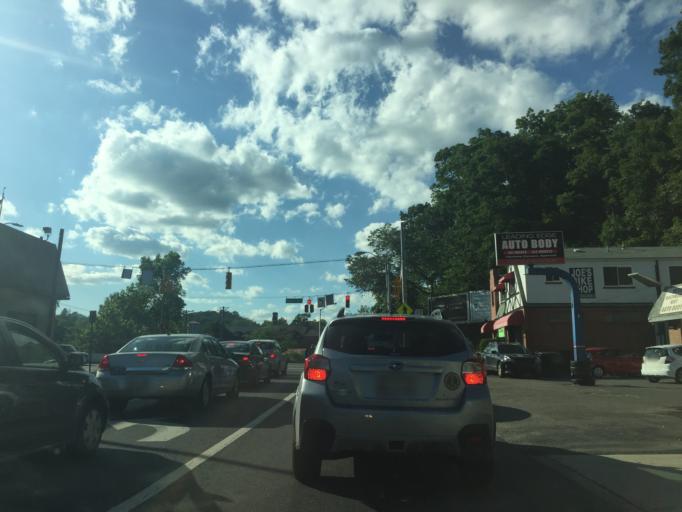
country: US
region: Maryland
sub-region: Baltimore County
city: Towson
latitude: 39.3668
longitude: -76.6479
